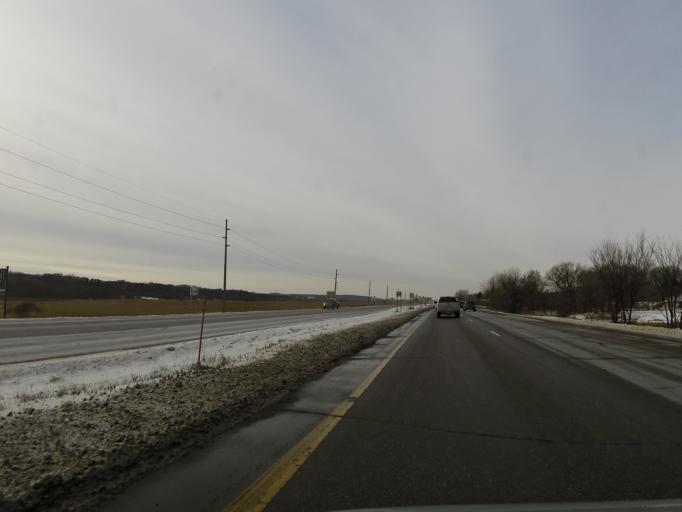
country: US
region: Minnesota
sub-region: Scott County
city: Jordan
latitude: 44.6706
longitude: -93.6398
